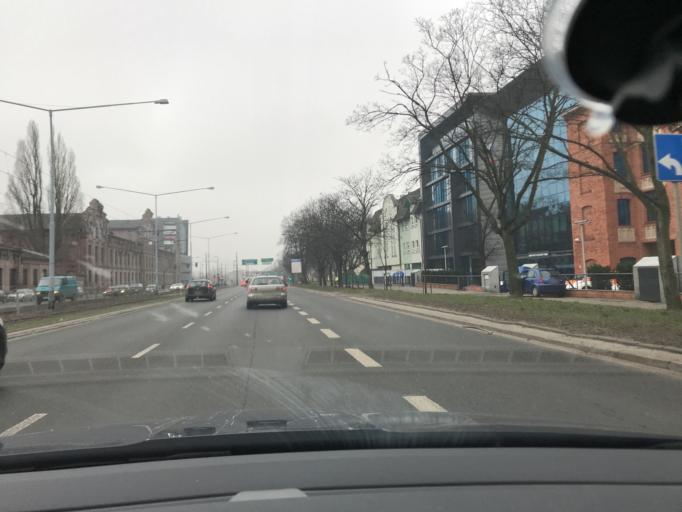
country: PL
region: Lodz Voivodeship
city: Lodz
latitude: 51.7644
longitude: 19.4842
